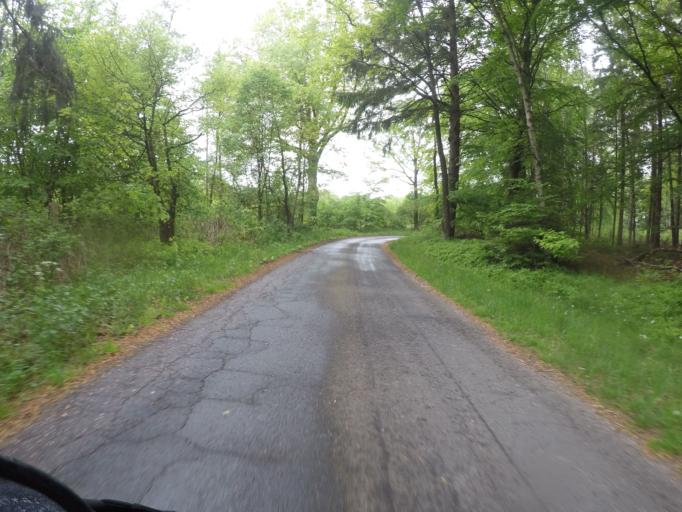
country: DE
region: Schleswig-Holstein
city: Heidmuhlen
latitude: 53.9611
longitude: 10.1012
